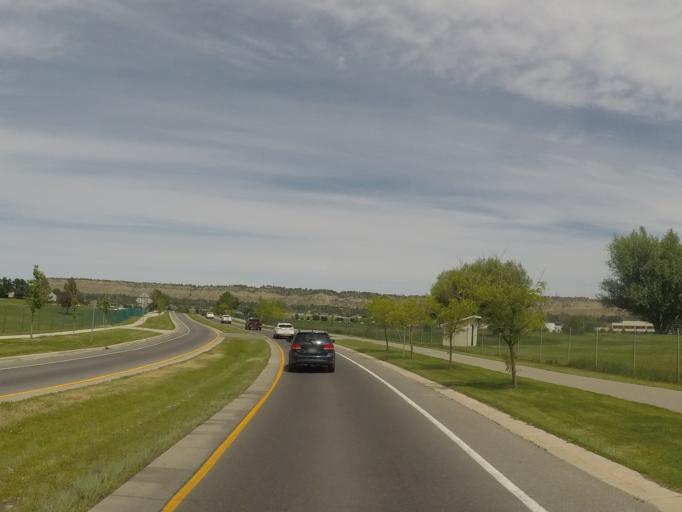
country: US
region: Montana
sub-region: Yellowstone County
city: Billings
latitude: 45.7784
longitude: -108.5973
